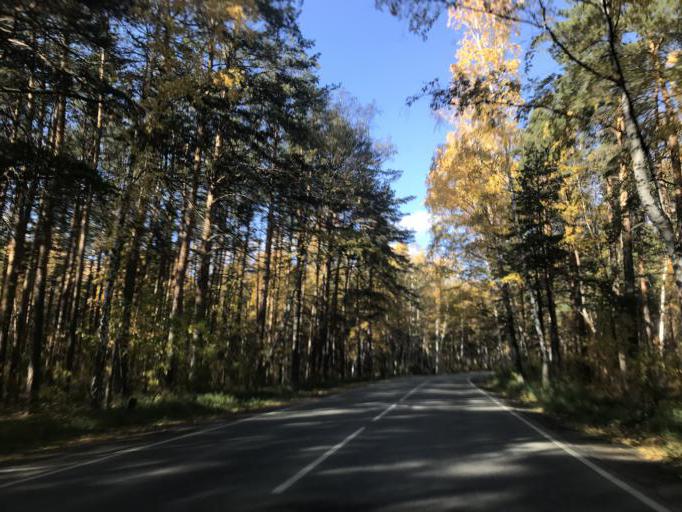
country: RU
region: Chelyabinsk
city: Dolgoderevenskoye
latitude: 55.2894
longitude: 61.3562
